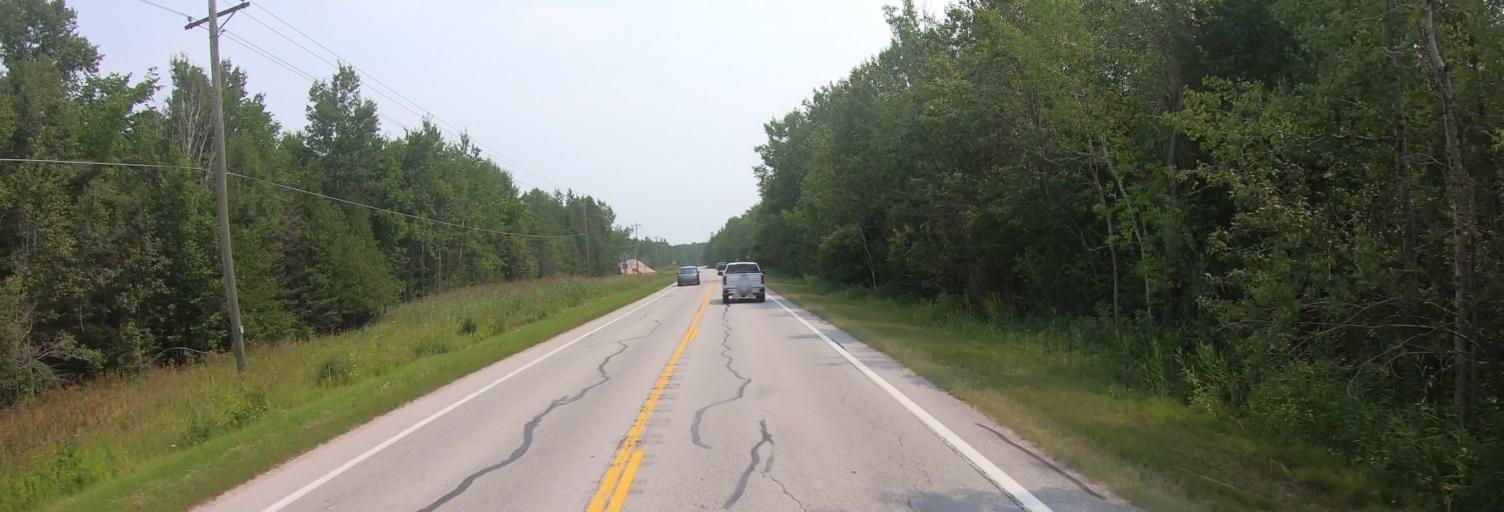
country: CA
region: Ontario
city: Thessalon
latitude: 45.9992
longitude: -83.7726
